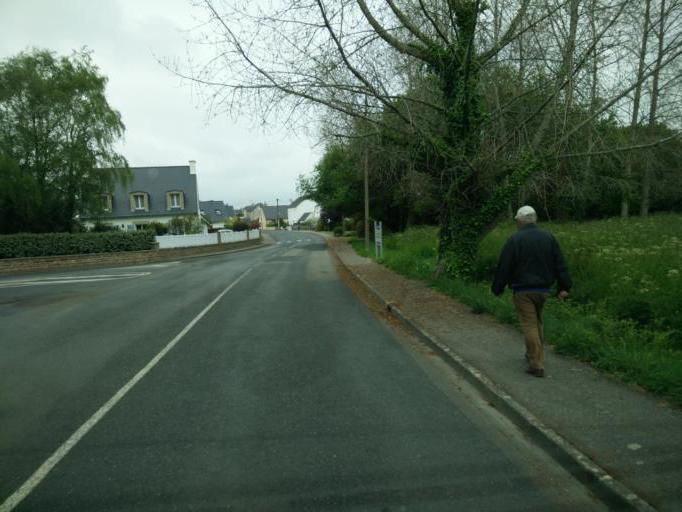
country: FR
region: Brittany
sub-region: Departement du Finistere
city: Loctudy
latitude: 47.8299
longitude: -4.1687
